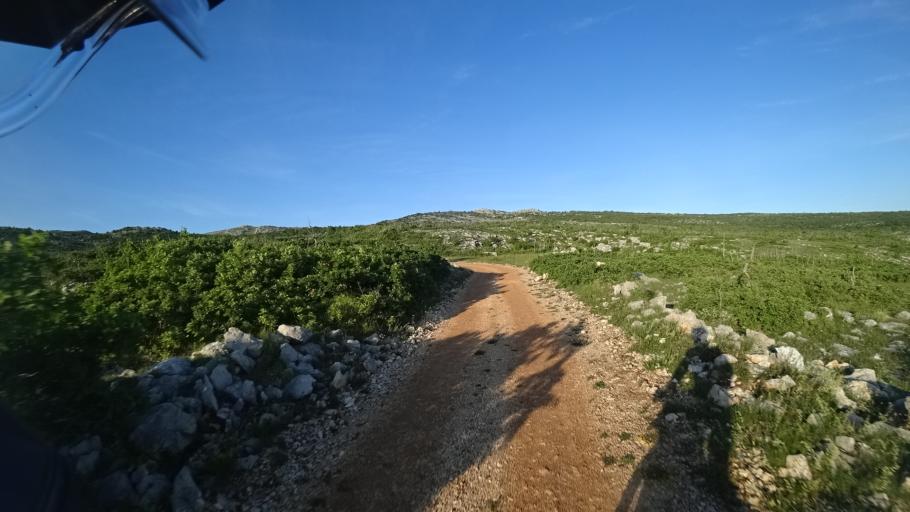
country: HR
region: Sibensko-Kniniska
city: Drnis
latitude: 43.8519
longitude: 16.3589
